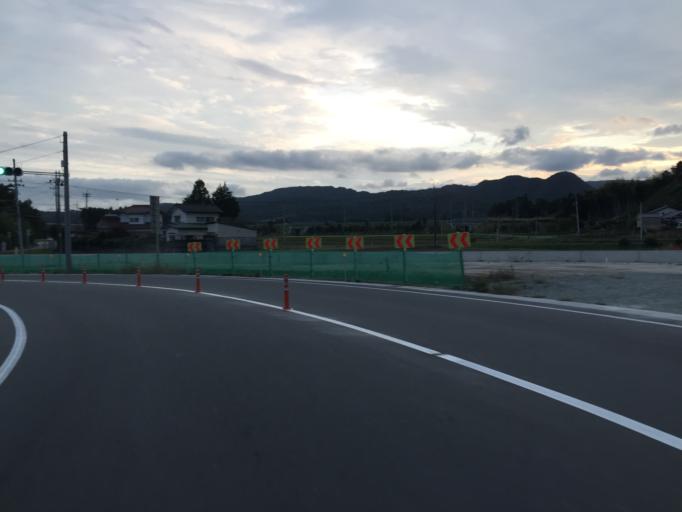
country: JP
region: Miyagi
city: Marumori
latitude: 37.7831
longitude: 140.8990
